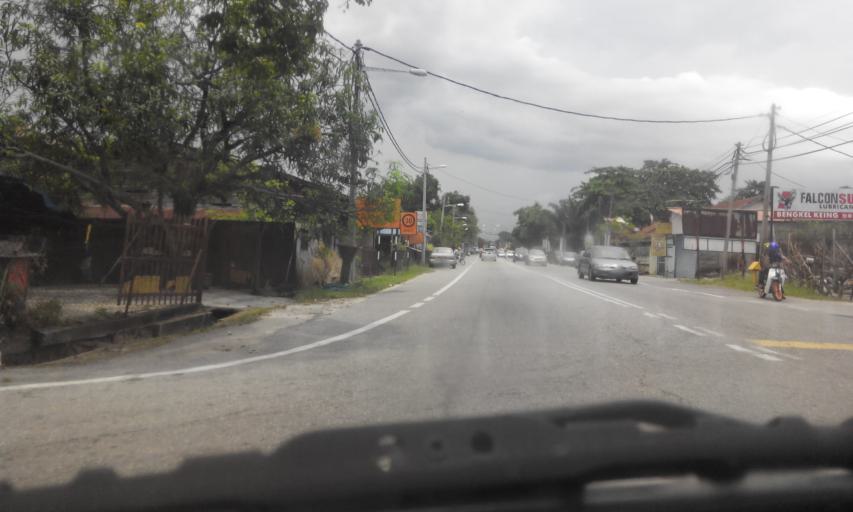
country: MY
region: Perak
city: Parit Buntar
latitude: 5.1274
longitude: 100.4929
